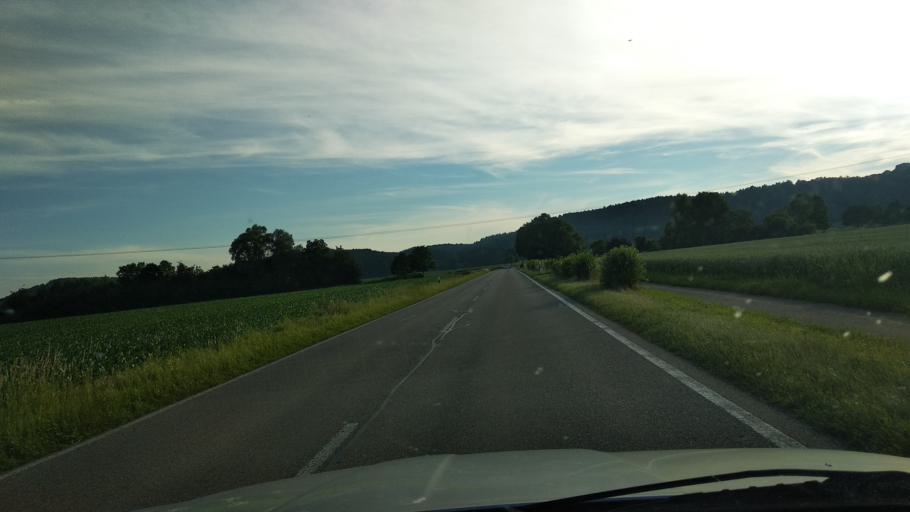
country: DE
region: Bavaria
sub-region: Swabia
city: Altenstadt
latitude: 48.1558
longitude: 10.0942
